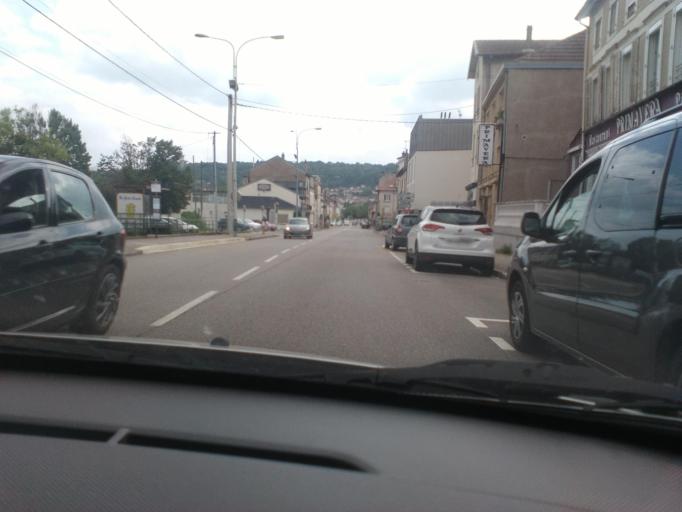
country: FR
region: Lorraine
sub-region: Departement de Meurthe-et-Moselle
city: Pompey
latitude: 48.7702
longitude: 6.1290
